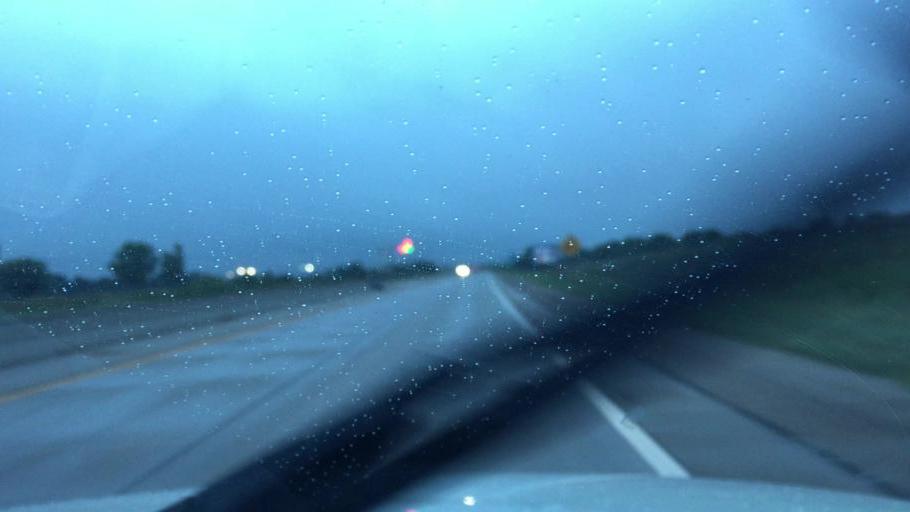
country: US
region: Kansas
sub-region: Neosho County
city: Chanute
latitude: 37.6588
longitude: -95.4796
